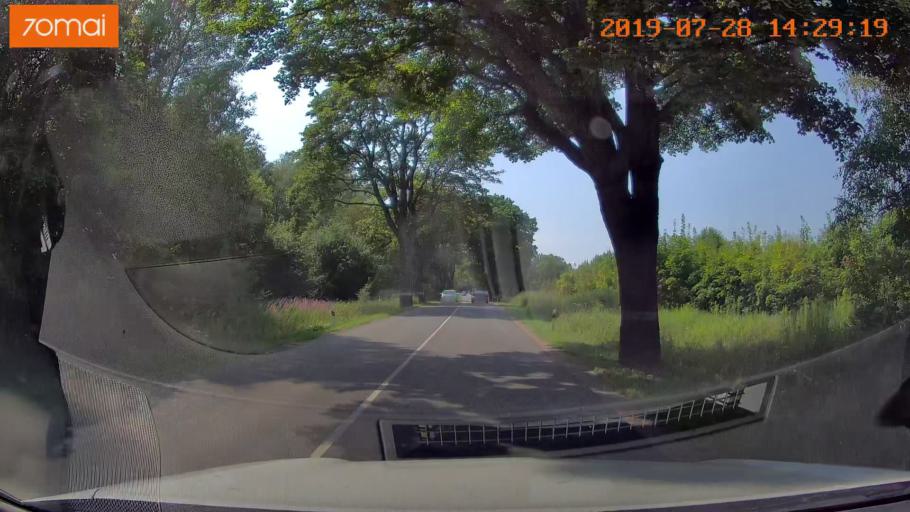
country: RU
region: Kaliningrad
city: Primorsk
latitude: 54.8097
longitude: 20.0704
